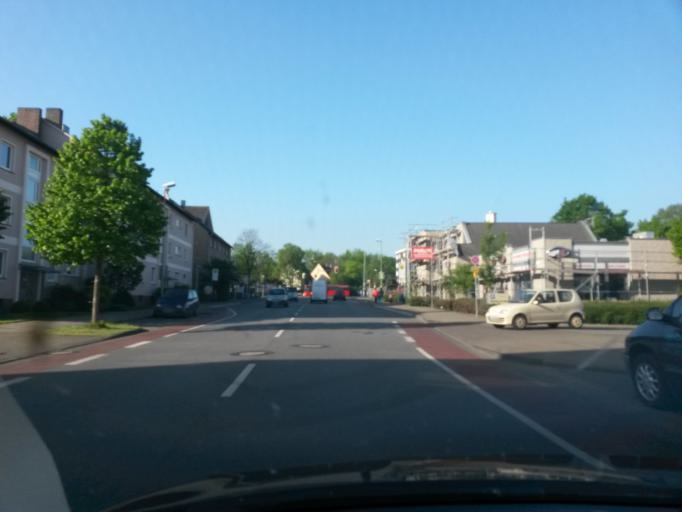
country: DE
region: North Rhine-Westphalia
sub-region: Regierungsbezirk Detmold
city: Bielefeld
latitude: 52.0135
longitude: 8.5650
